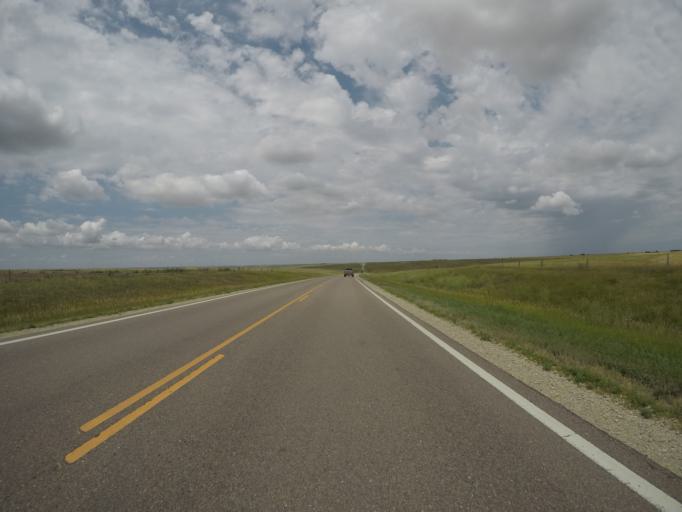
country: US
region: Kansas
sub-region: Rawlins County
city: Atwood
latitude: 39.7338
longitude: -101.0556
